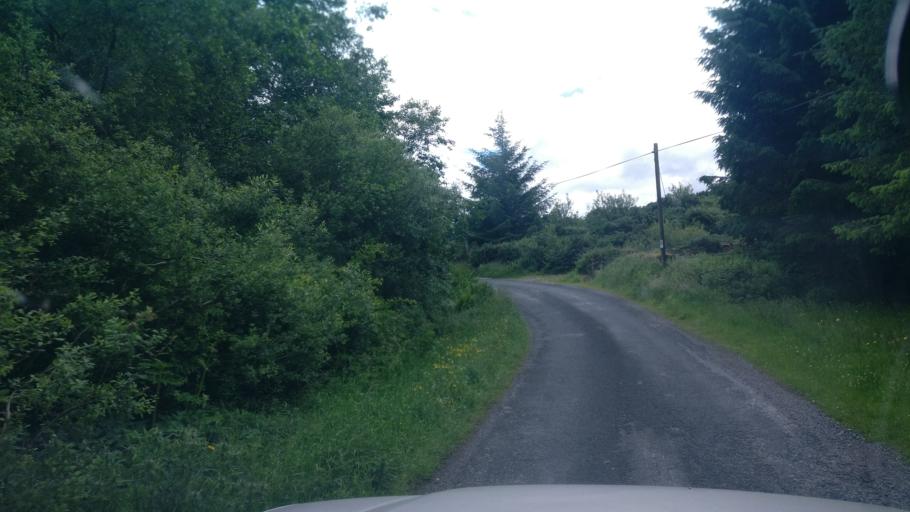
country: IE
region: Connaught
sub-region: County Galway
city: Loughrea
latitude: 53.1477
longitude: -8.5661
